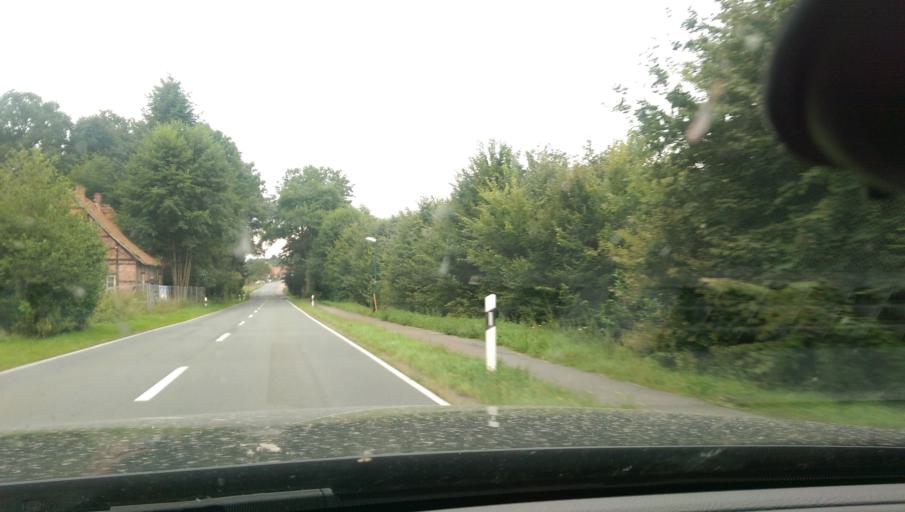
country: DE
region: Lower Saxony
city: Rehburg-Loccum
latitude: 52.4606
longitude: 9.1675
